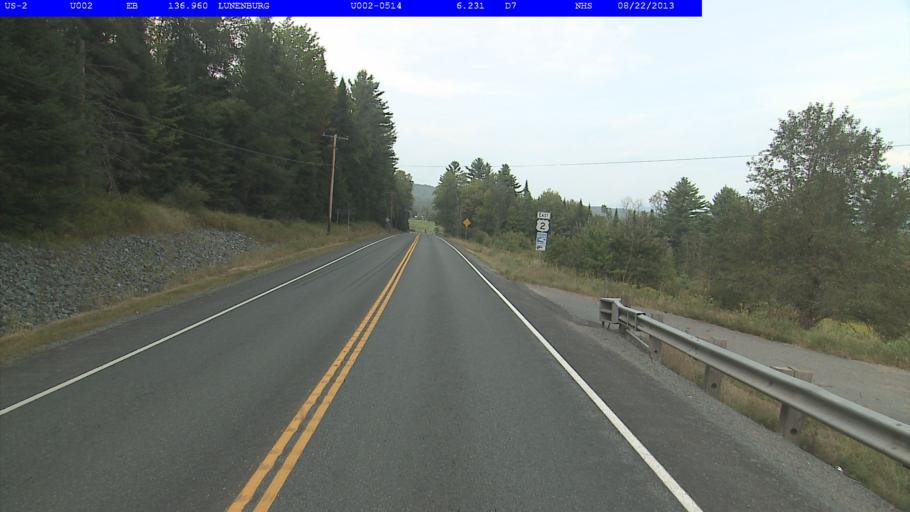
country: US
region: New Hampshire
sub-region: Coos County
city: Lancaster
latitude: 44.4661
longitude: -71.6522
